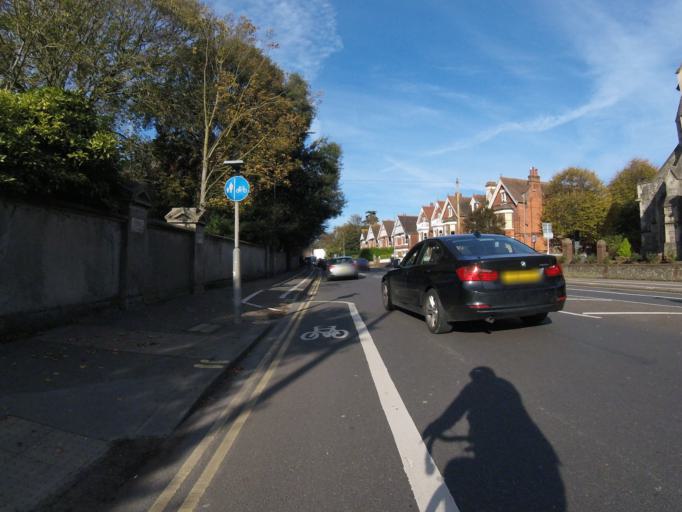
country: GB
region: England
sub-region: Brighton and Hove
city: Brighton
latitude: 50.8441
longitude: -0.1515
